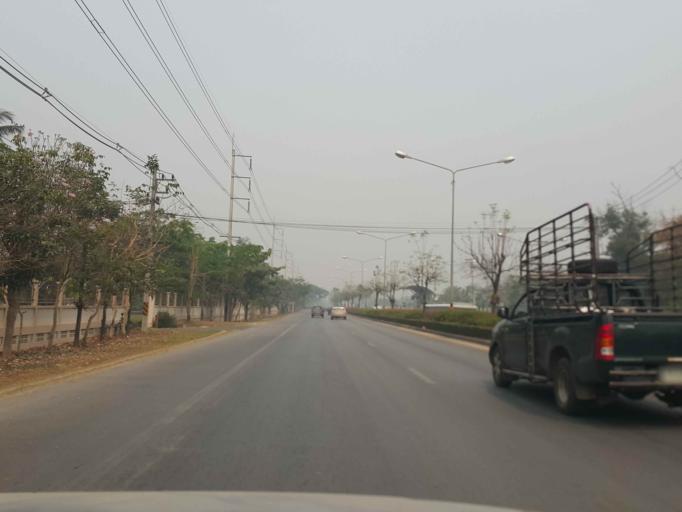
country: TH
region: Chiang Mai
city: San Sai
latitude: 18.9062
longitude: 99.0029
